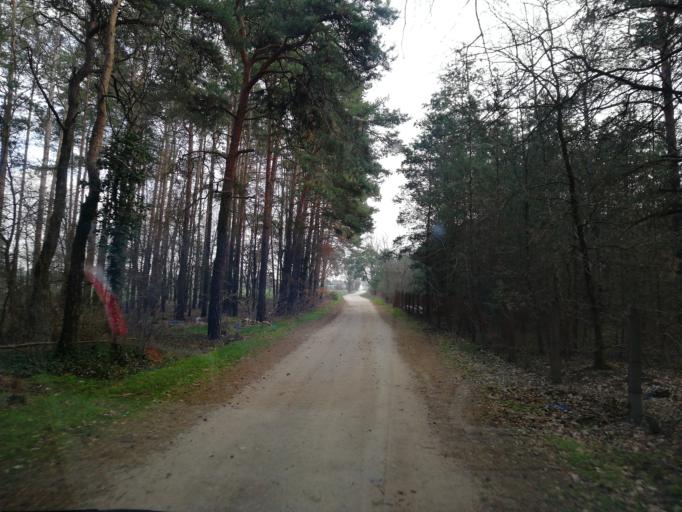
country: DE
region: Brandenburg
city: Finsterwalde
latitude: 51.6583
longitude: 13.6964
